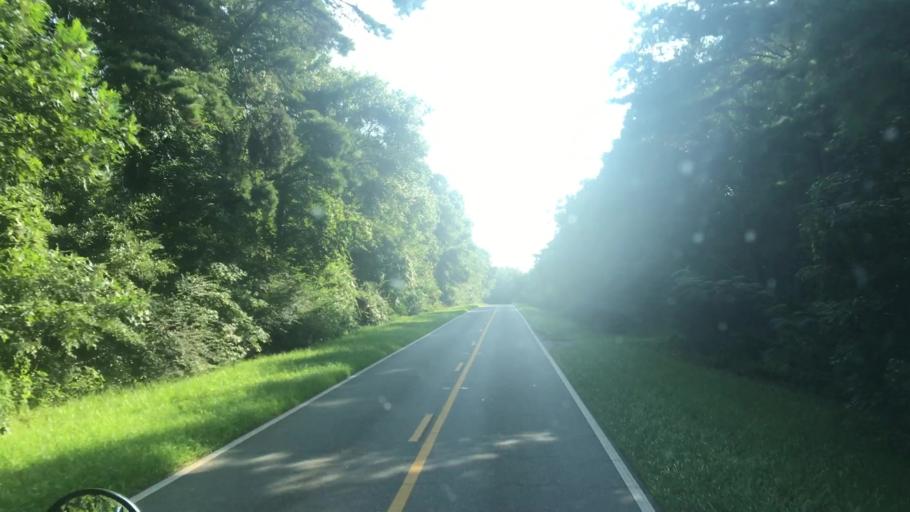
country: US
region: Florida
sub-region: Gadsden County
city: Quincy
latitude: 30.6711
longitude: -84.5457
